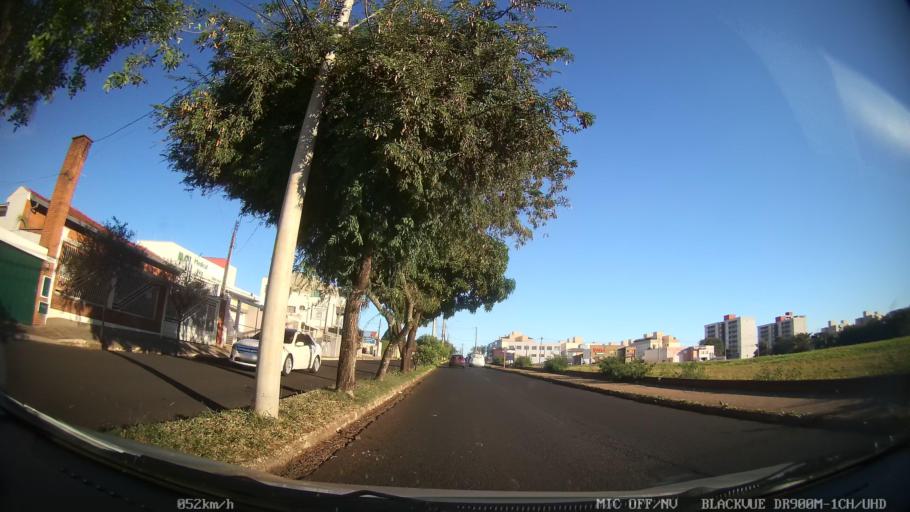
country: BR
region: Sao Paulo
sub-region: Araraquara
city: Araraquara
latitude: -21.7556
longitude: -48.1631
